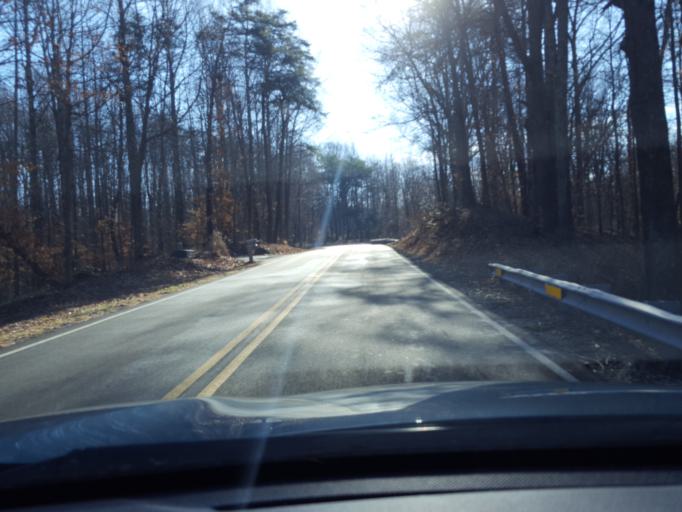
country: US
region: Maryland
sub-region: Calvert County
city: Chesapeake Beach
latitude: 38.6480
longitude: -76.5637
